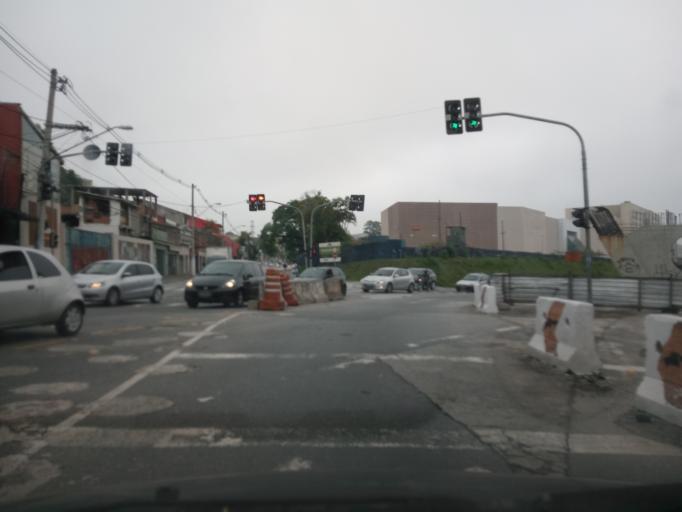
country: BR
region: Sao Paulo
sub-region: Sao Bernardo Do Campo
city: Sao Bernardo do Campo
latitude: -23.7219
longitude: -46.5395
